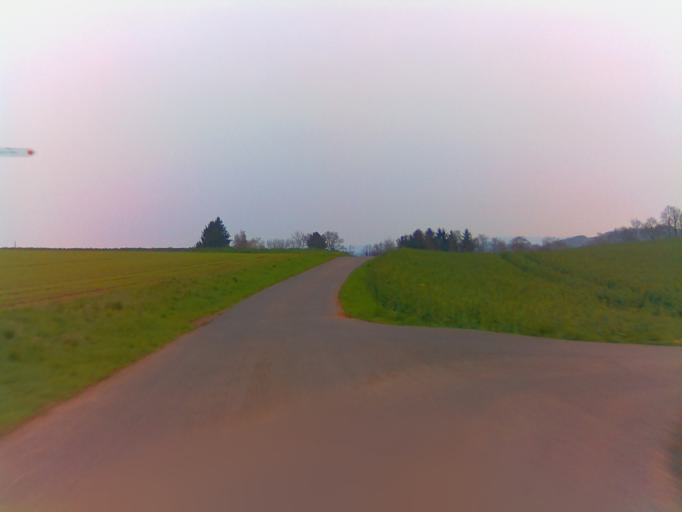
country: DE
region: Rheinland-Pfalz
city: Hoppstadten-Weiersbach
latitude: 49.6269
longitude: 7.2134
